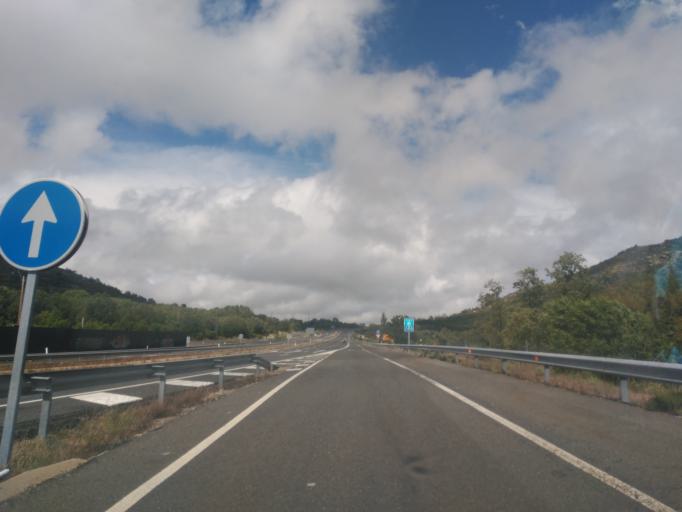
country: ES
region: Castille and Leon
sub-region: Provincia de Salamanca
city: Vallejera de Riofrio
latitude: 40.4121
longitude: -5.7189
